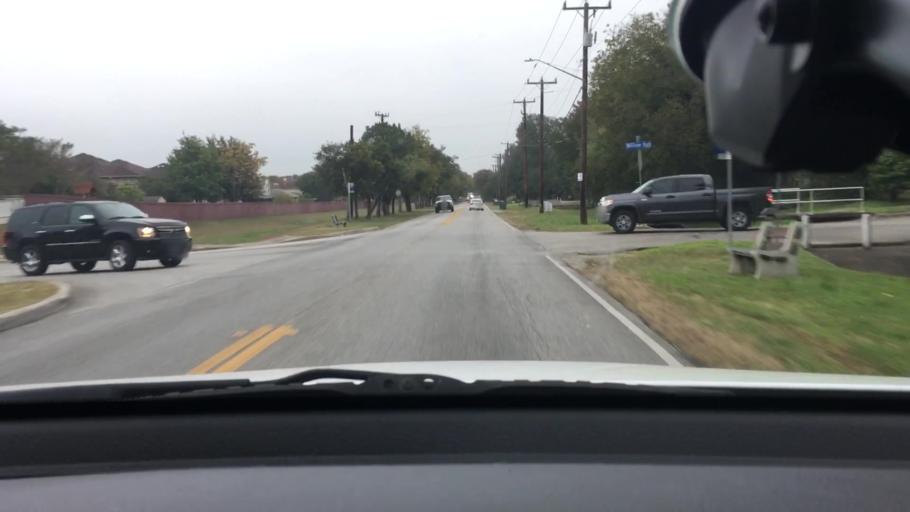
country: US
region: Texas
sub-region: Bexar County
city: Live Oak
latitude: 29.5933
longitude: -98.3654
